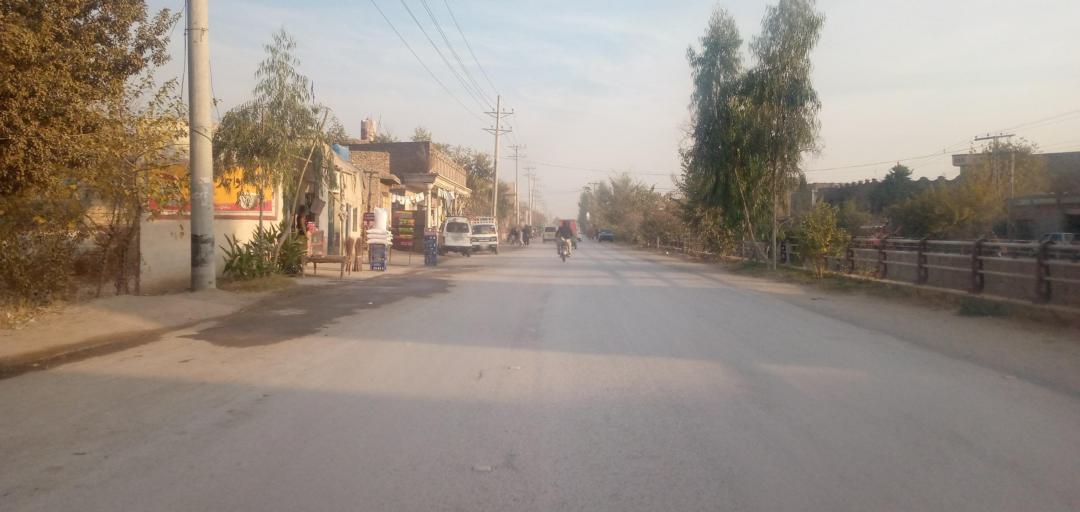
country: PK
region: Khyber Pakhtunkhwa
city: Peshawar
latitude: 33.9724
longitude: 71.5316
